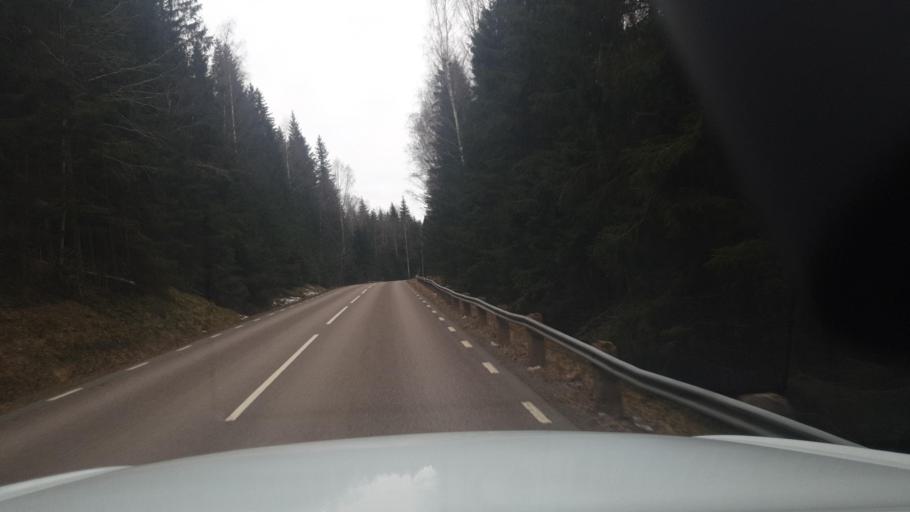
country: SE
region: Vaermland
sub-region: Sunne Kommun
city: Sunne
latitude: 59.8285
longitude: 12.9810
